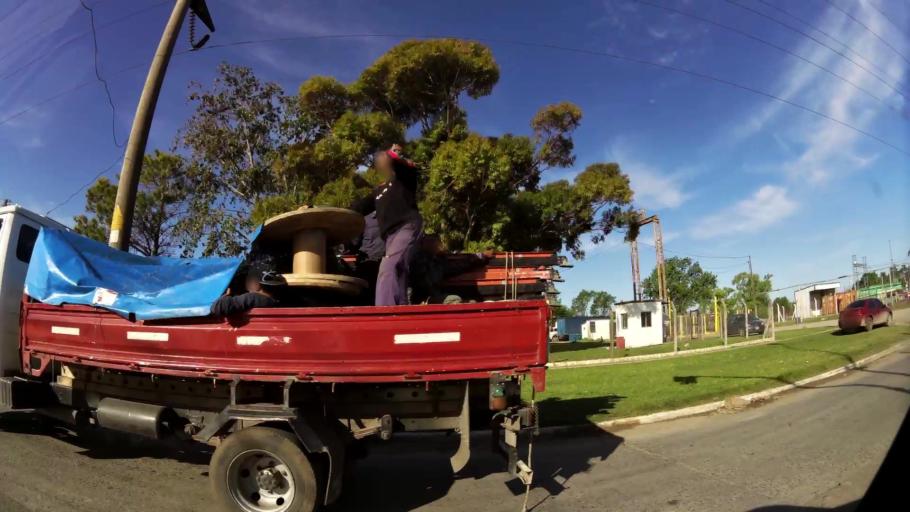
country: AR
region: Buenos Aires
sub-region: Partido de Quilmes
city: Quilmes
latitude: -34.8005
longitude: -58.2182
